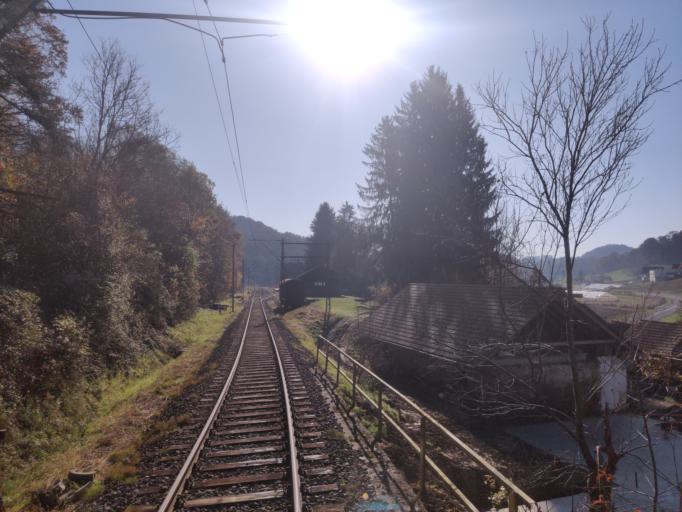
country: AT
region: Styria
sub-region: Politischer Bezirk Suedoststeiermark
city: Maierdorf
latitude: 46.8888
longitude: 15.8544
